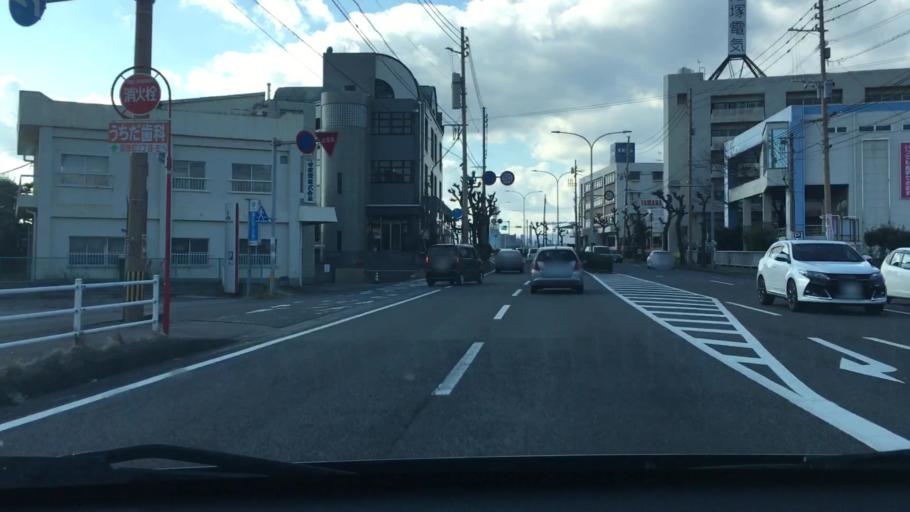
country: JP
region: Oita
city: Oita
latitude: 33.2319
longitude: 131.6278
